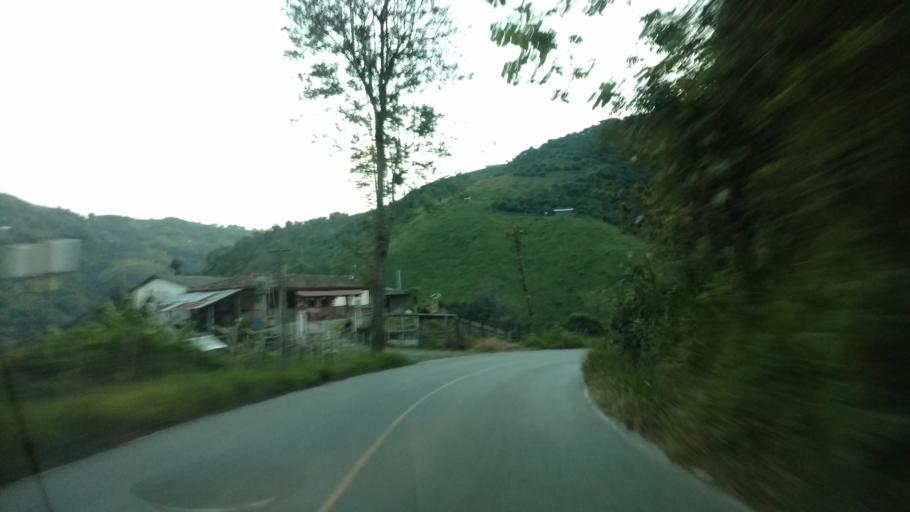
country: CO
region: Caldas
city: Aranzazu
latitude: 5.2634
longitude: -75.4981
